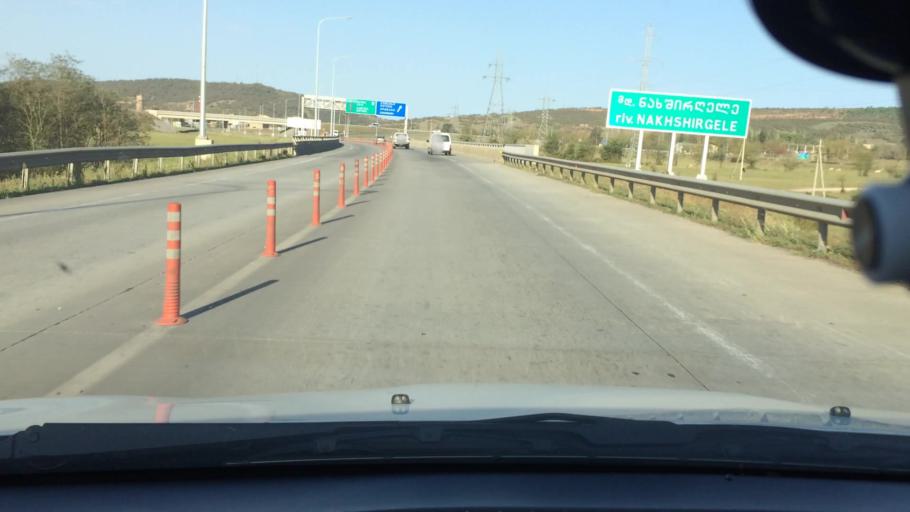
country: GE
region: Imereti
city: Kutaisi
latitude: 42.2108
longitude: 42.8250
